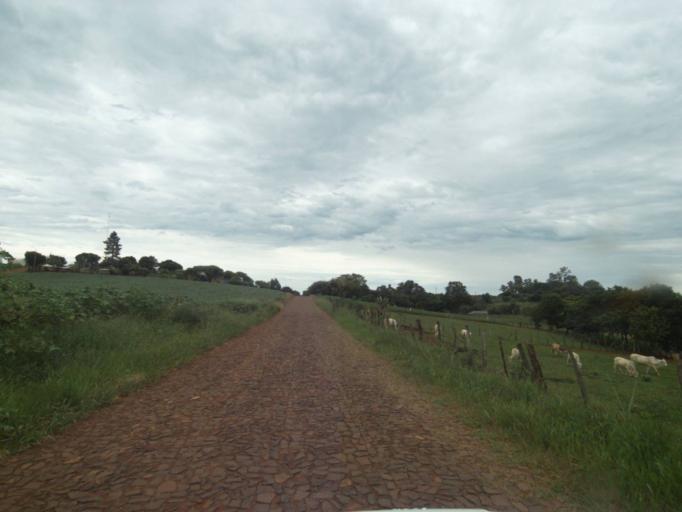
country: BR
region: Parana
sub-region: Guaraniacu
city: Guaraniacu
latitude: -24.9248
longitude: -52.9381
